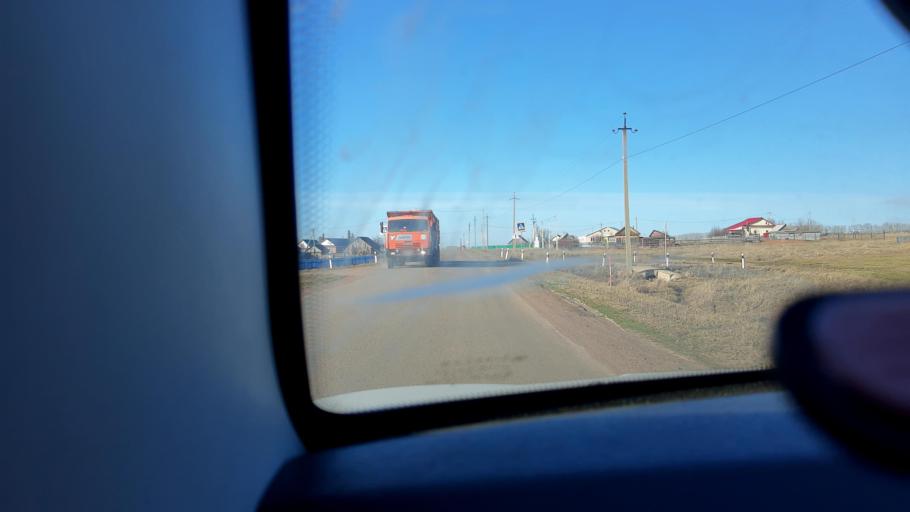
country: RU
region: Bashkortostan
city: Asanovo
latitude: 54.8415
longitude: 55.4579
